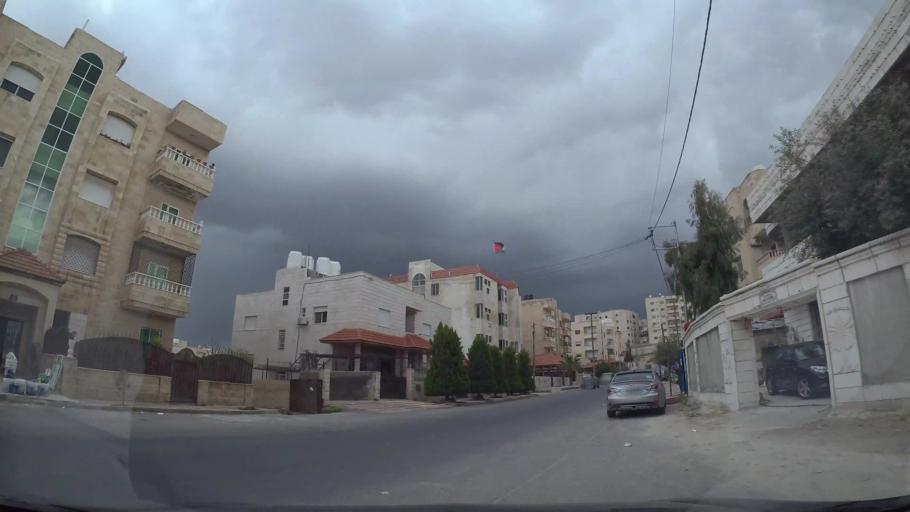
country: JO
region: Amman
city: Amman
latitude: 32.0076
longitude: 35.9502
